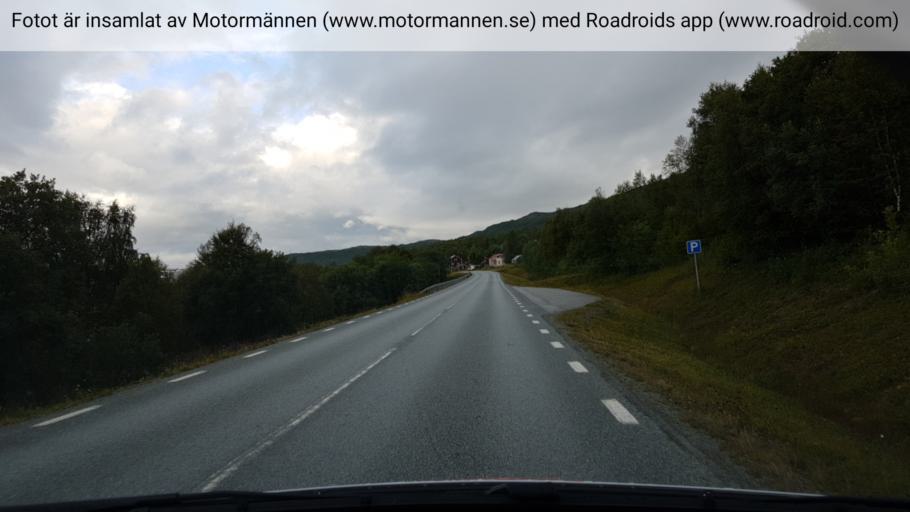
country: NO
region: Nordland
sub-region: Rana
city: Mo i Rana
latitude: 66.0460
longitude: 14.9729
